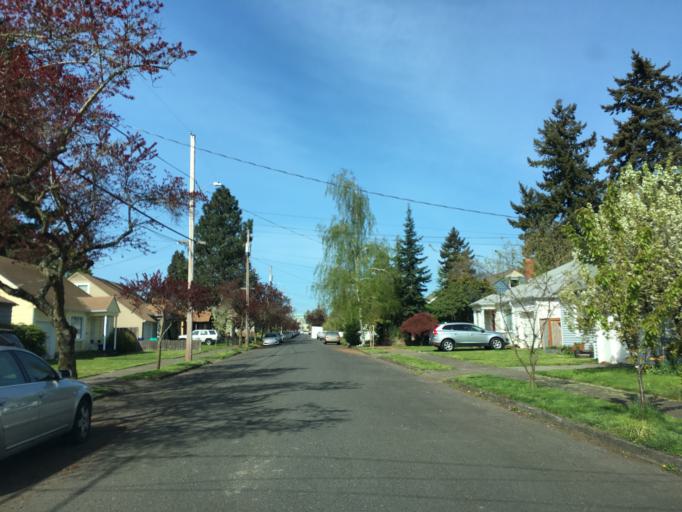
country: US
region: Oregon
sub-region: Multnomah County
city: Lents
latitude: 45.5296
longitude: -122.5739
